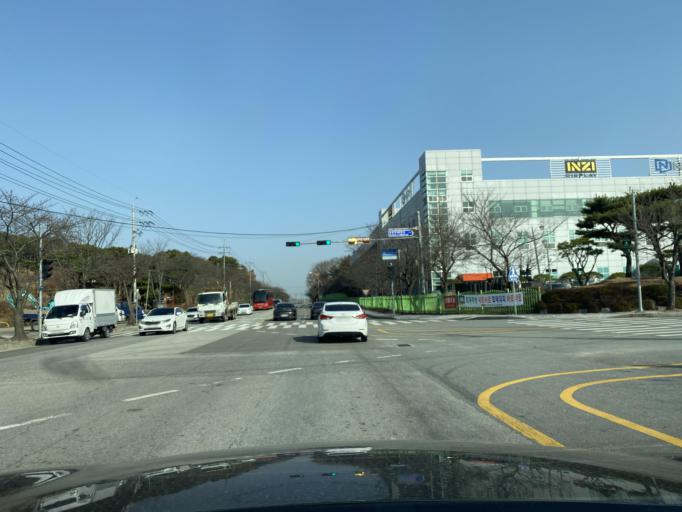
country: KR
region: Chungcheongnam-do
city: Yesan
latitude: 36.7145
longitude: 126.8422
